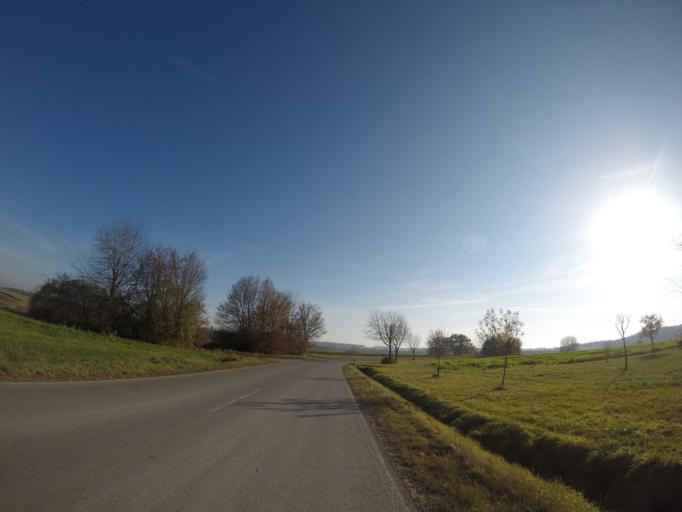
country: DE
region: Baden-Wuerttemberg
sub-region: Tuebingen Region
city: Grundsheim
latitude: 48.1821
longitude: 9.6639
